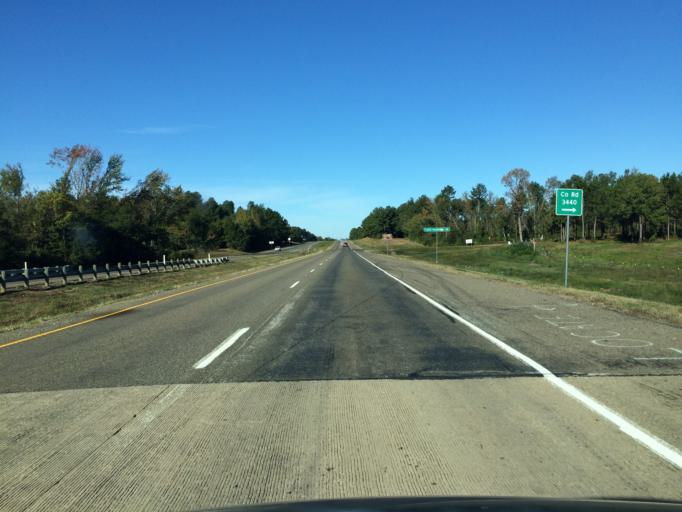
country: US
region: Texas
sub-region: Wood County
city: Hawkins
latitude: 32.5980
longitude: -95.2558
